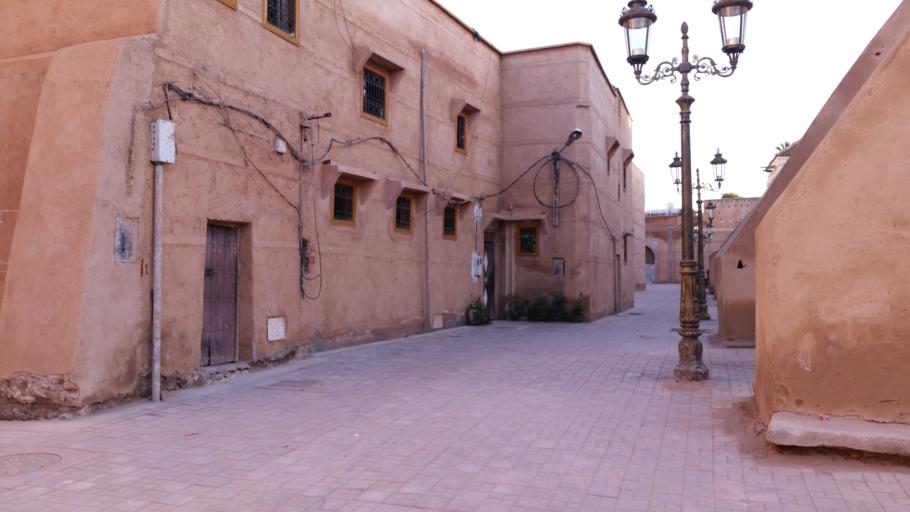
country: MA
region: Marrakech-Tensift-Al Haouz
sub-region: Marrakech
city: Marrakesh
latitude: 31.6181
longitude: -7.9885
